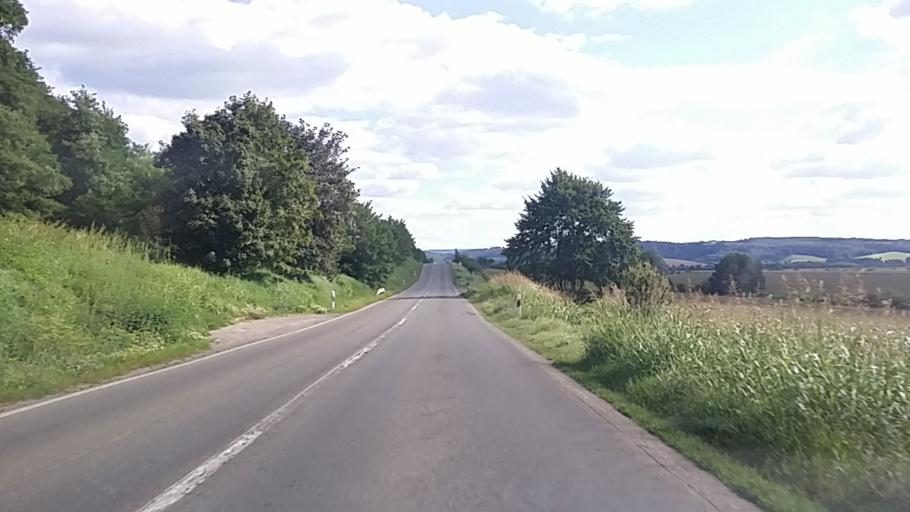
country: HU
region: Baranya
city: Sasd
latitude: 46.2342
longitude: 18.1213
